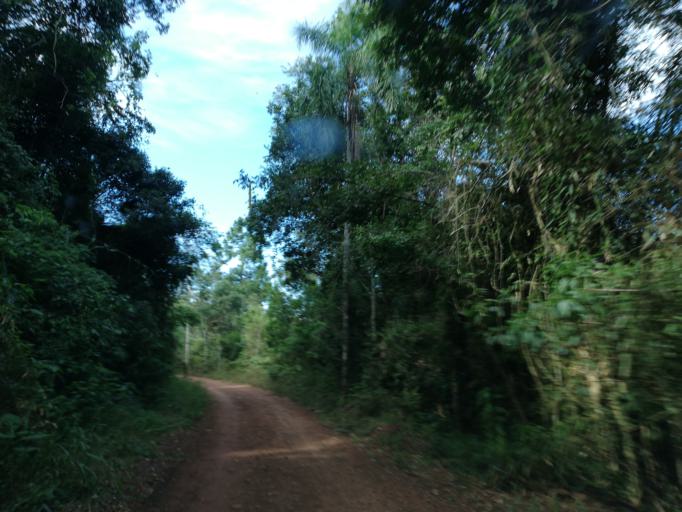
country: AR
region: Misiones
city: Dos de Mayo
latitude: -27.0160
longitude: -54.4380
